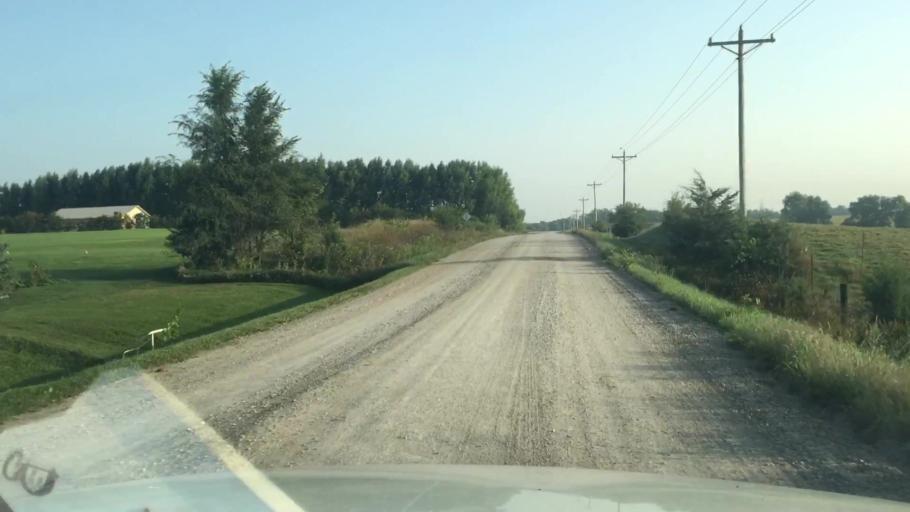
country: US
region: Iowa
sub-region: Story County
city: Huxley
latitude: 41.8943
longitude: -93.5809
